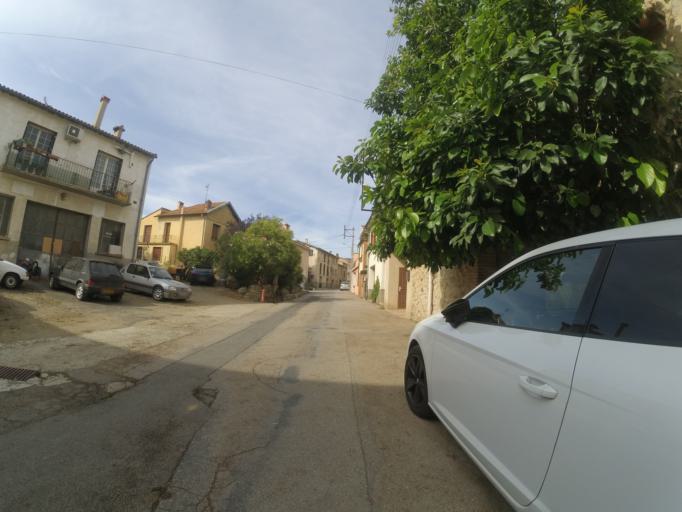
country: FR
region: Languedoc-Roussillon
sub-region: Departement des Pyrenees-Orientales
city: Millas
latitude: 42.6578
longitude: 2.6742
